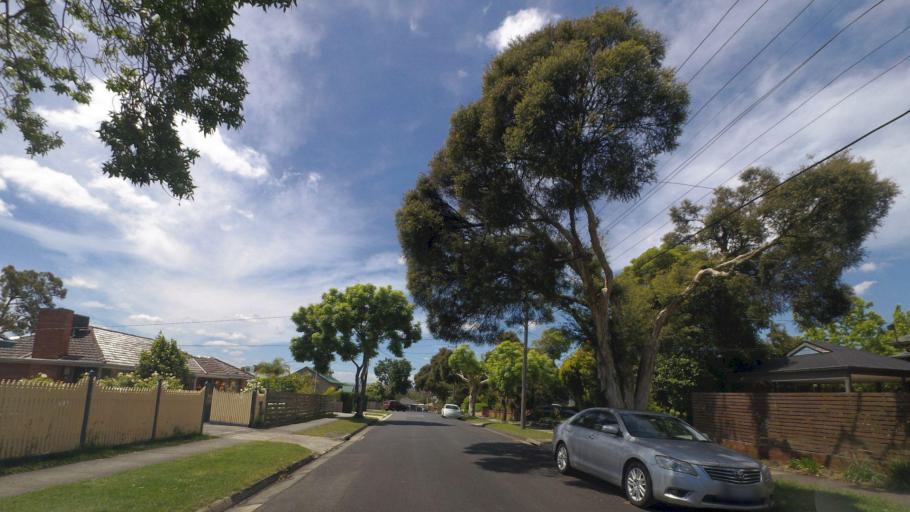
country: AU
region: Victoria
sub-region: Whitehorse
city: Vermont
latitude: -37.8376
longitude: 145.2041
